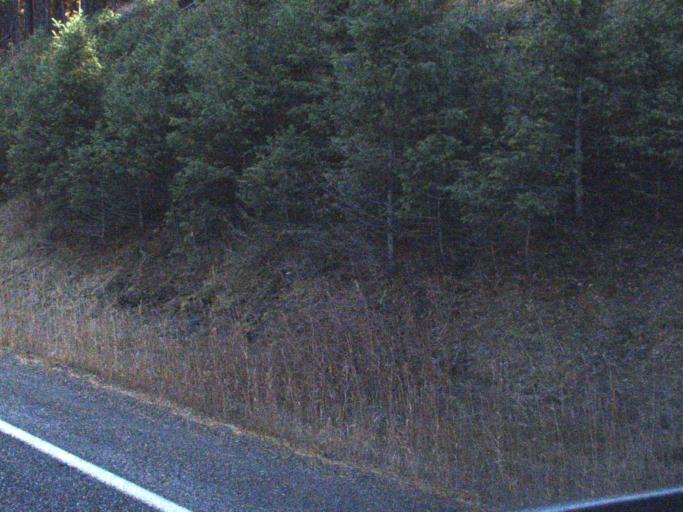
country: US
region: Washington
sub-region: Ferry County
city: Republic
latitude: 48.6534
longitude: -118.7917
